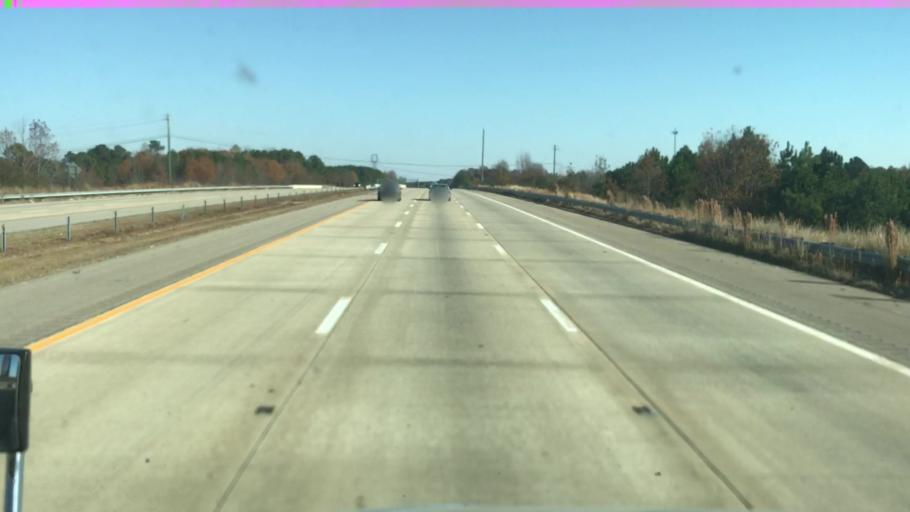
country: US
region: North Carolina
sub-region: Wake County
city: Knightdale
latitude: 35.7669
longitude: -78.4678
